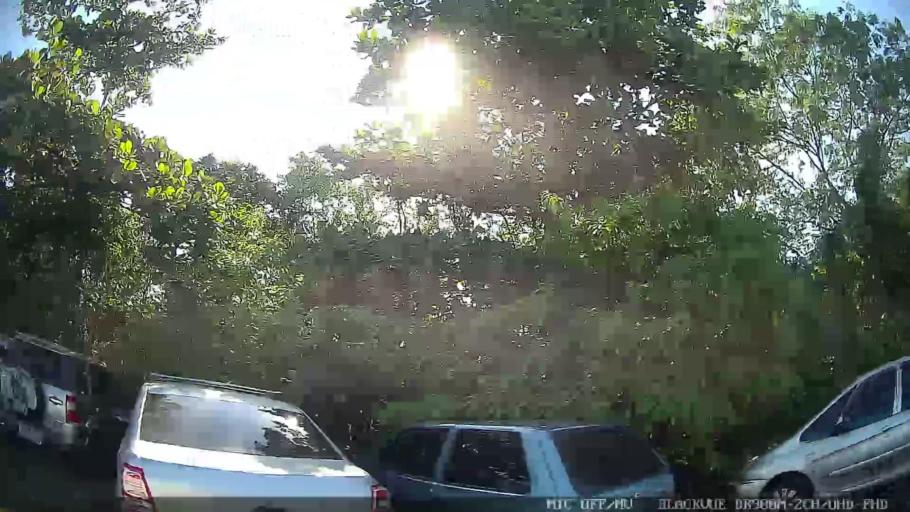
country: BR
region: Sao Paulo
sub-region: Guaruja
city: Guaruja
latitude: -24.0004
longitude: -46.2924
